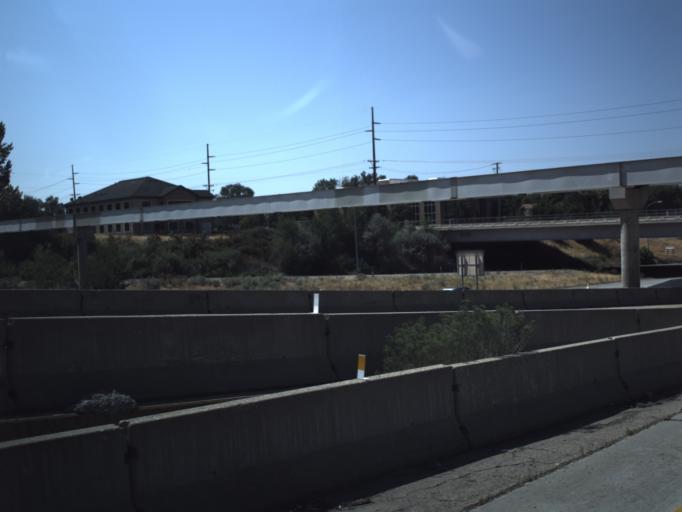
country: US
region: Utah
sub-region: Salt Lake County
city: Midvale
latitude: 40.6306
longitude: -111.8643
